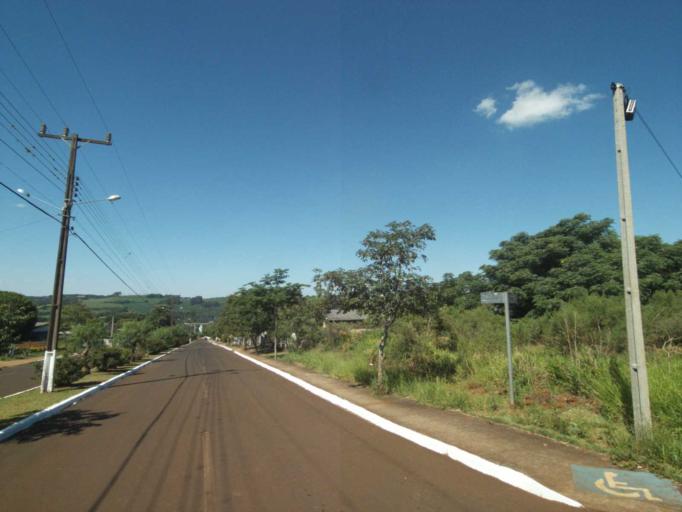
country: BR
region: Parana
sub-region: Laranjeiras Do Sul
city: Laranjeiras do Sul
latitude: -25.3840
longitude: -52.2067
